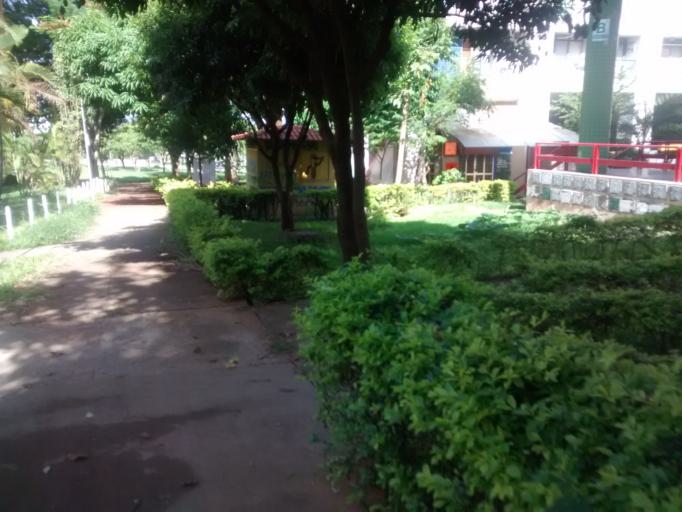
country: BR
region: Federal District
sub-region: Brasilia
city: Brasilia
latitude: -15.7460
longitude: -47.8918
